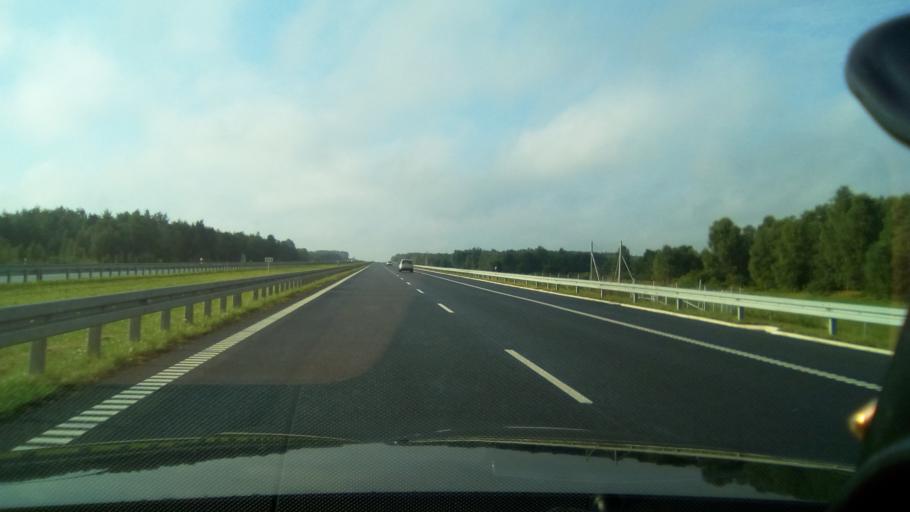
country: PL
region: Silesian Voivodeship
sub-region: Powiat czestochowski
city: Konopiska
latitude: 50.7277
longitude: 19.0571
